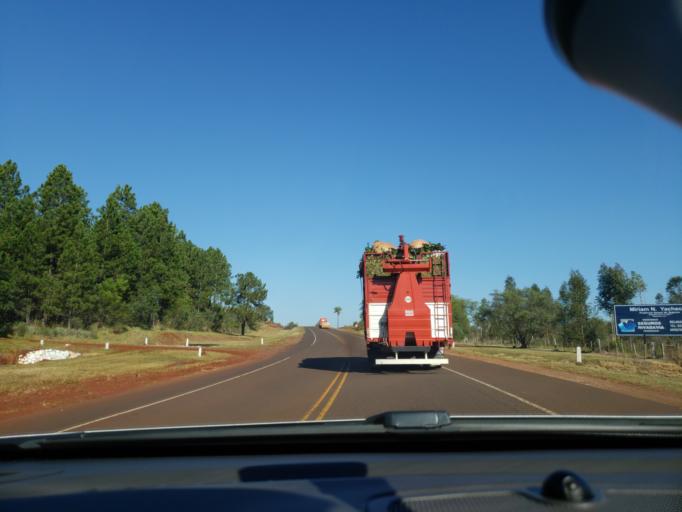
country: AR
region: Misiones
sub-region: Departamento de Apostoles
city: San Jose
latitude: -27.8267
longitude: -55.7708
